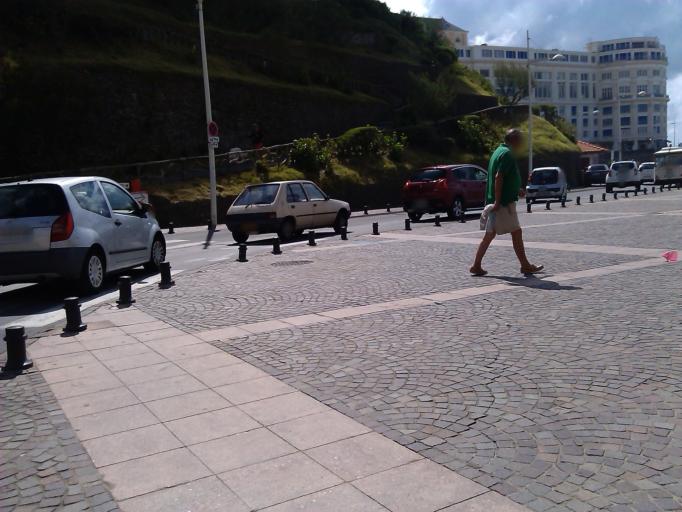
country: FR
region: Aquitaine
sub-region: Departement des Pyrenees-Atlantiques
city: Biarritz
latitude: 43.4833
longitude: -1.5597
